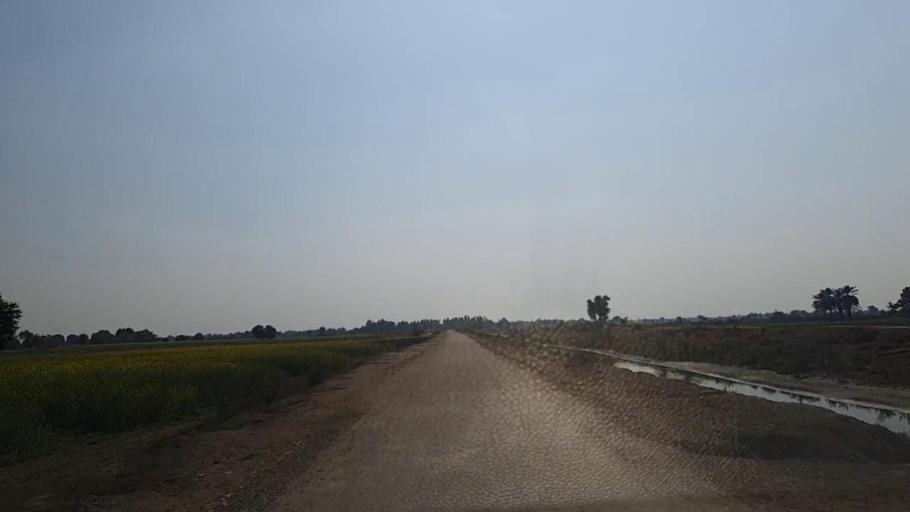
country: PK
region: Sindh
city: Nawabshah
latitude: 26.2549
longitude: 68.5030
